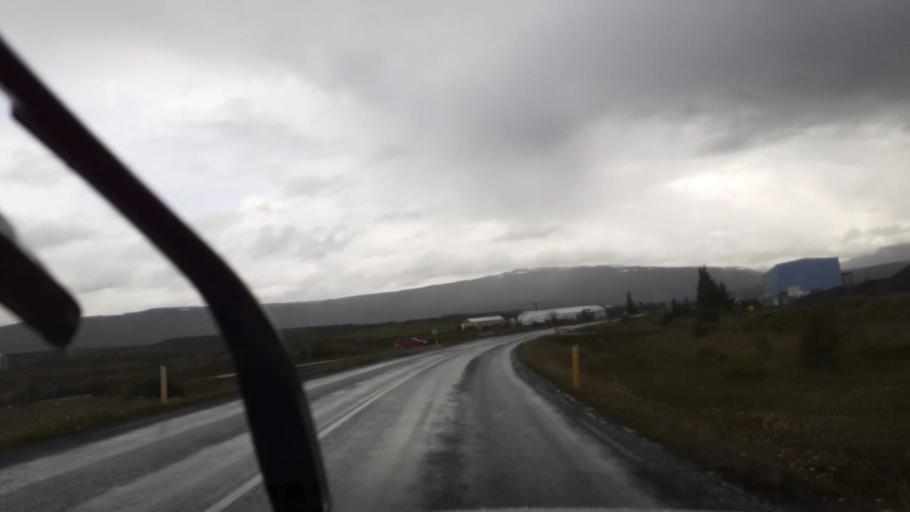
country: IS
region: East
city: Egilsstadir
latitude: 65.2988
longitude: -14.4487
